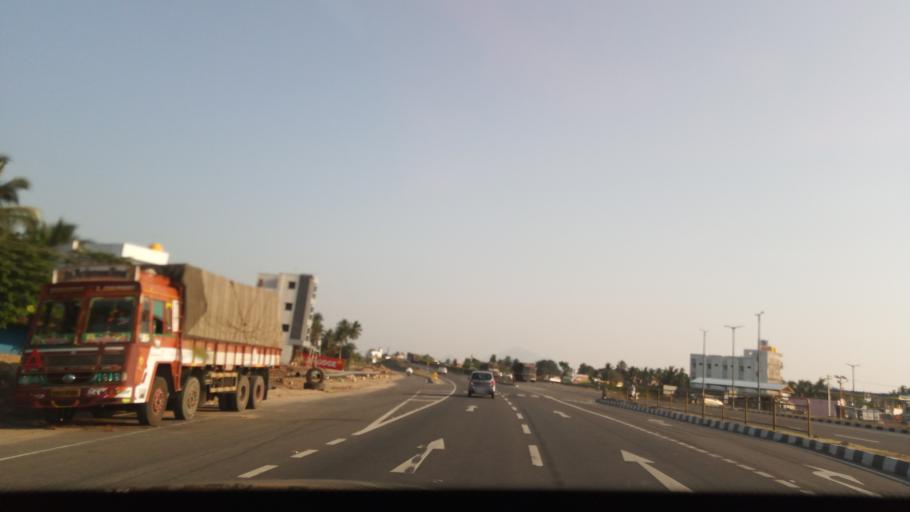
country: IN
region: Tamil Nadu
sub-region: Dharmapuri
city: Dharmapuri
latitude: 12.2580
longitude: 78.1980
